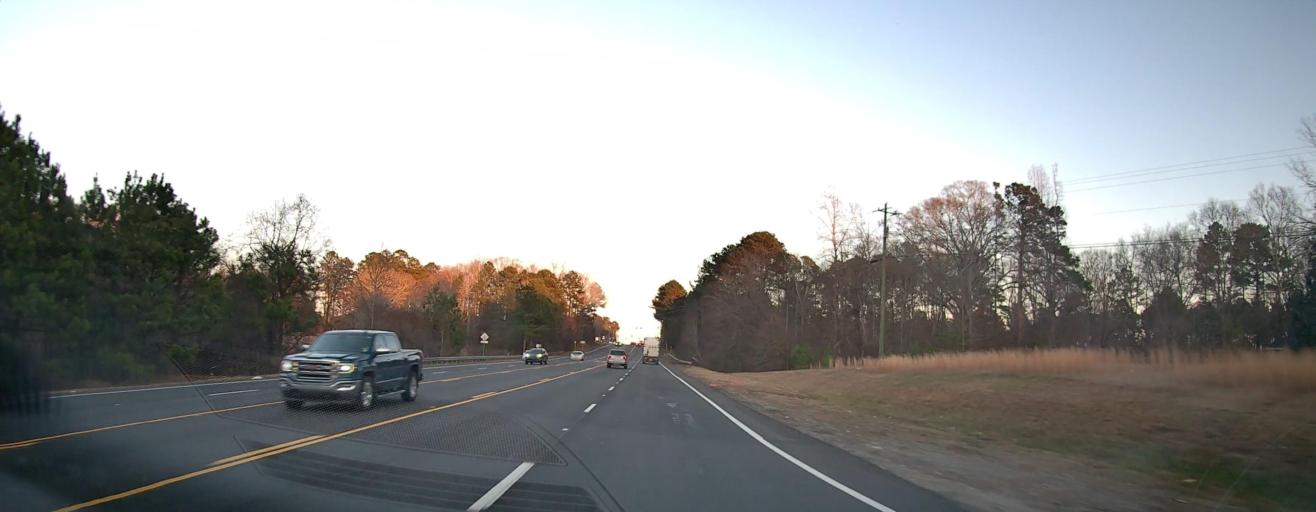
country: US
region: Georgia
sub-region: Clayton County
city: Riverdale
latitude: 33.5511
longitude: -84.4698
